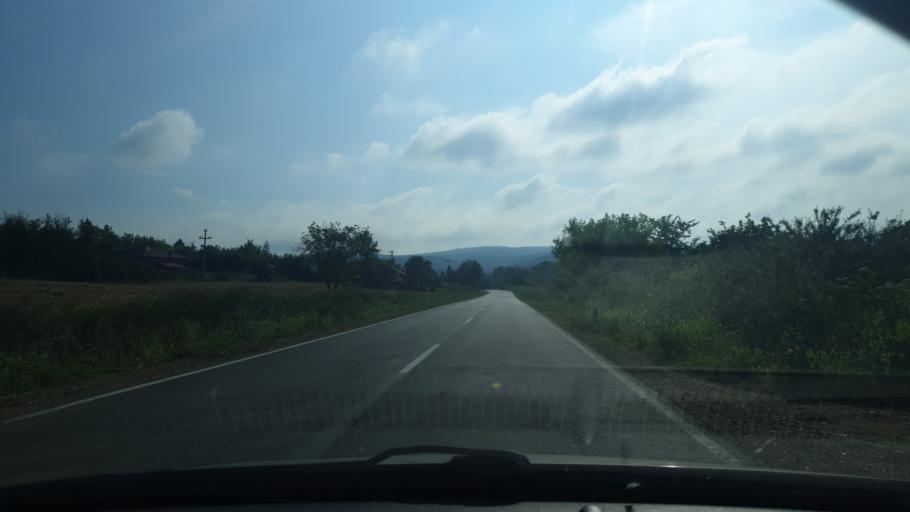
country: RS
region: Central Serbia
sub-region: Pomoravski Okrug
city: Cuprija
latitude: 43.9562
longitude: 21.4635
